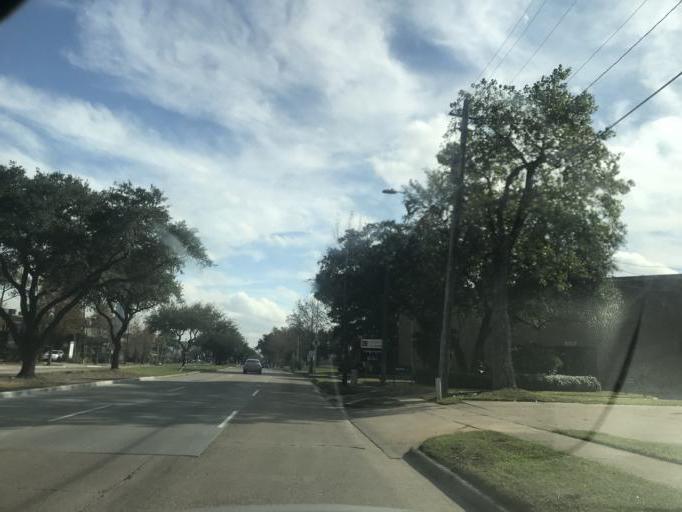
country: US
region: Texas
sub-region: Harris County
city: Hunters Creek Village
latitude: 29.7317
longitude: -95.4896
